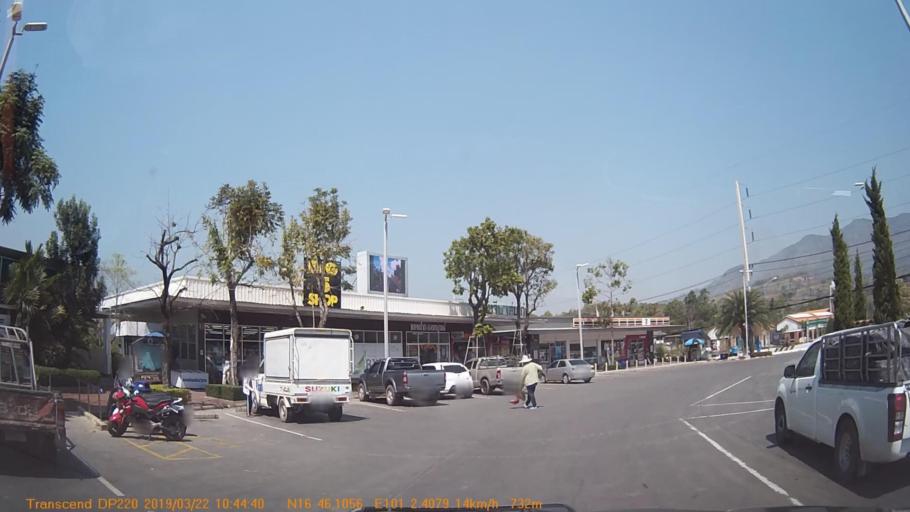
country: TH
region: Phetchabun
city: Khao Kho
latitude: 16.7685
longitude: 101.0401
